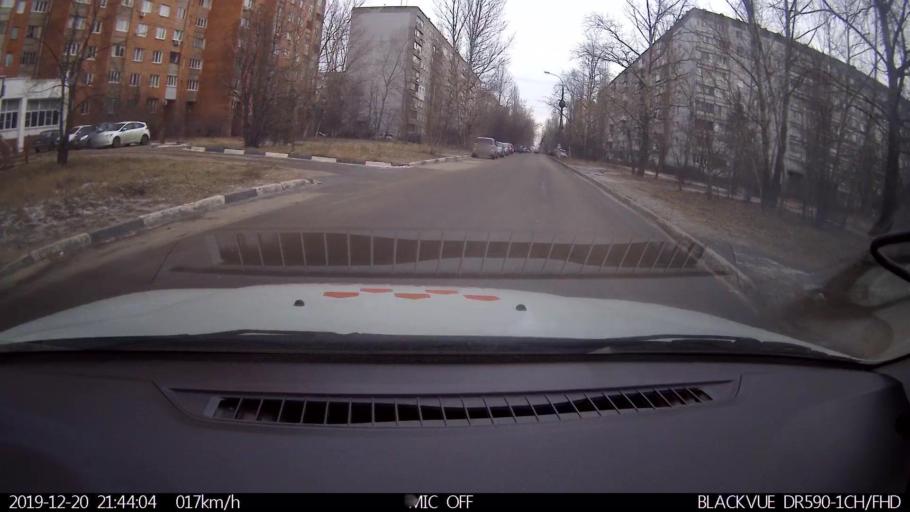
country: RU
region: Nizjnij Novgorod
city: Nizhniy Novgorod
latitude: 56.3329
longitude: 43.9359
